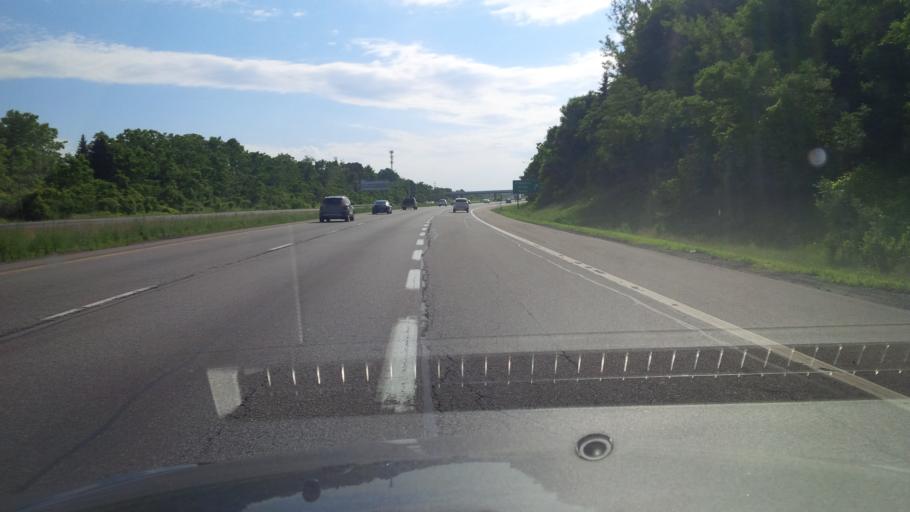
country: CA
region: Ontario
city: Ancaster
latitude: 43.2068
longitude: -79.9776
